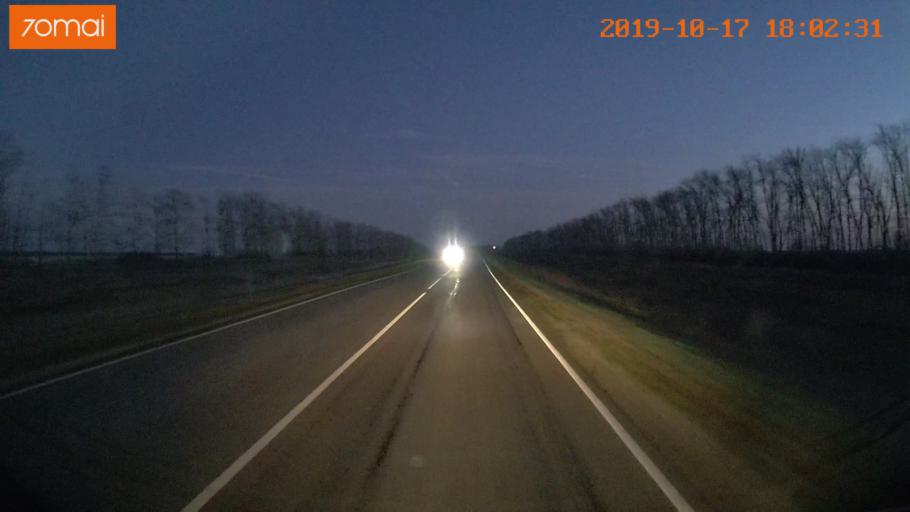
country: RU
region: Tula
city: Kurkino
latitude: 53.5060
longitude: 38.6148
